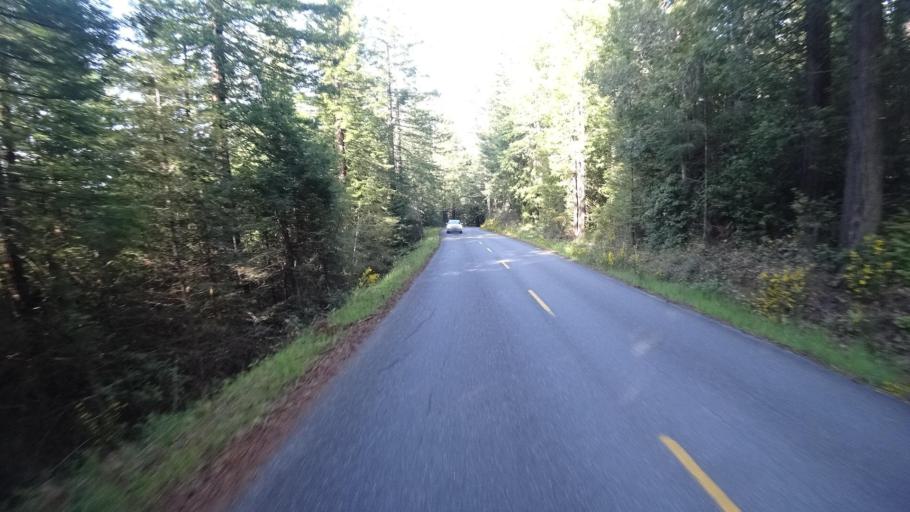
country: US
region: California
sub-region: Humboldt County
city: Bayside
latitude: 40.7581
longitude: -124.0244
